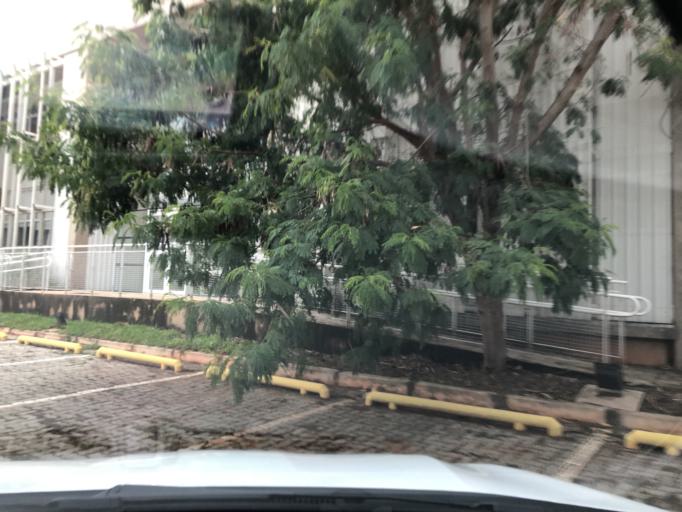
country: BR
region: Federal District
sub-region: Brasilia
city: Brasilia
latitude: -15.7694
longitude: -47.8664
